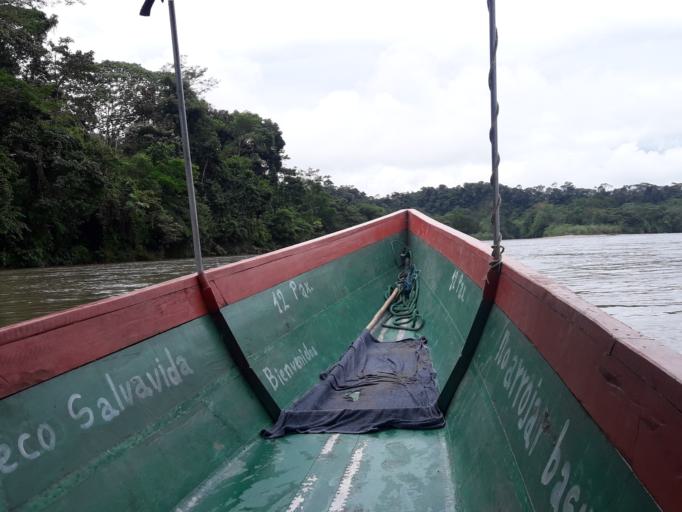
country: EC
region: Napo
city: Tena
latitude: -1.0359
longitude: -77.6610
